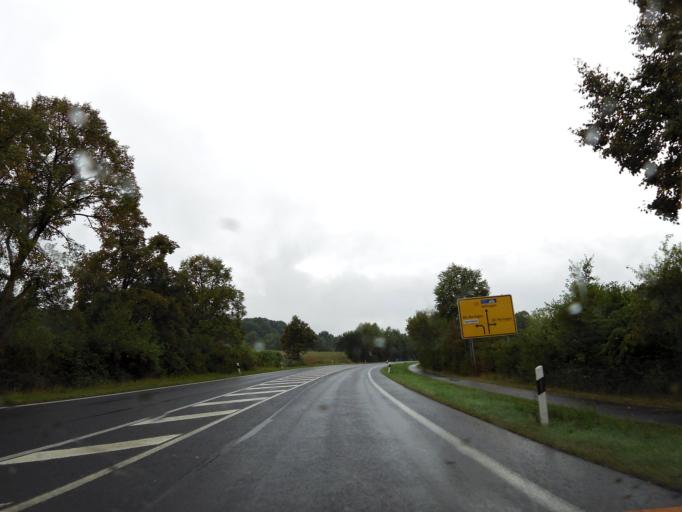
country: DE
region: Lower Saxony
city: Waake
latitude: 51.5584
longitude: 10.0144
